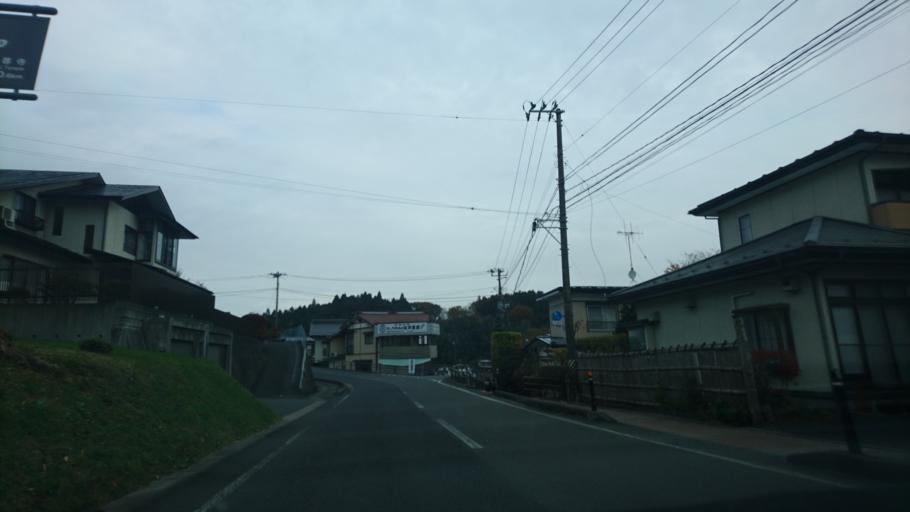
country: JP
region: Iwate
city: Ichinoseki
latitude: 38.9941
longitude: 141.1118
